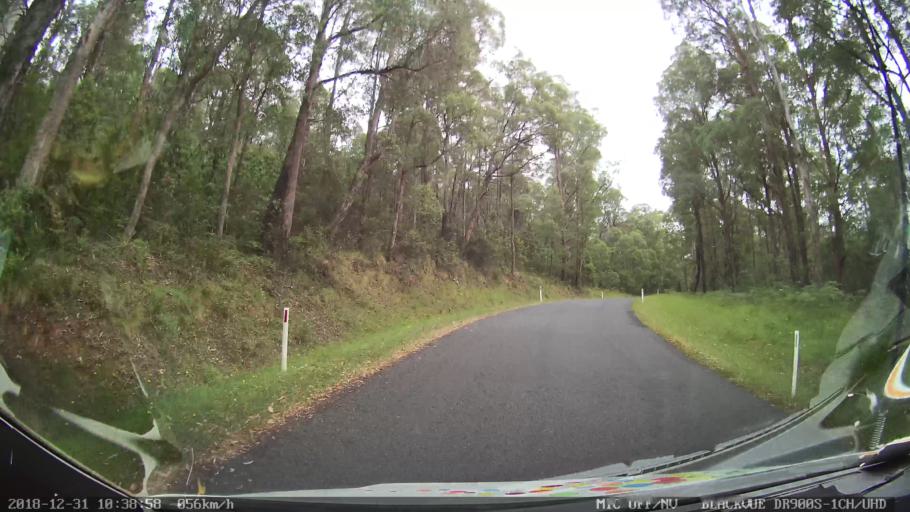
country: AU
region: New South Wales
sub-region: Snowy River
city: Jindabyne
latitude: -36.4033
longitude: 148.1765
